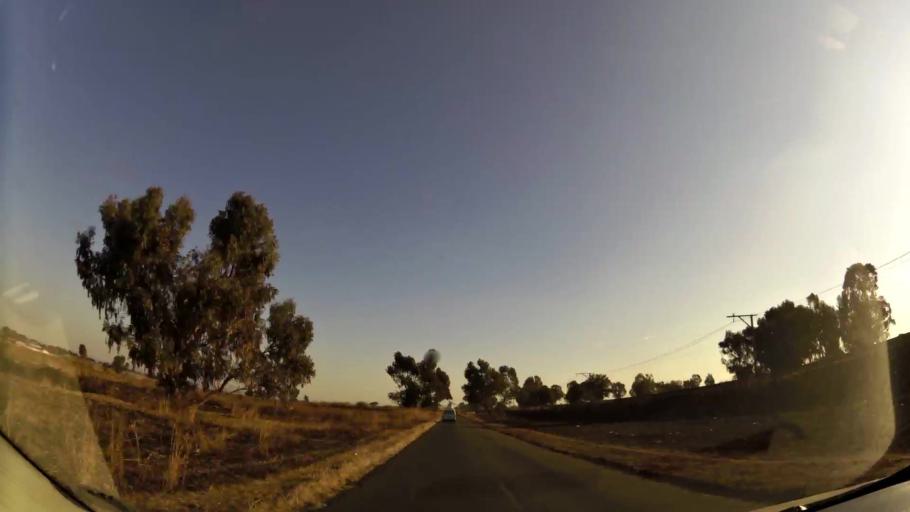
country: ZA
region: Gauteng
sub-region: West Rand District Municipality
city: Randfontein
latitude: -26.1965
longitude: 27.6785
